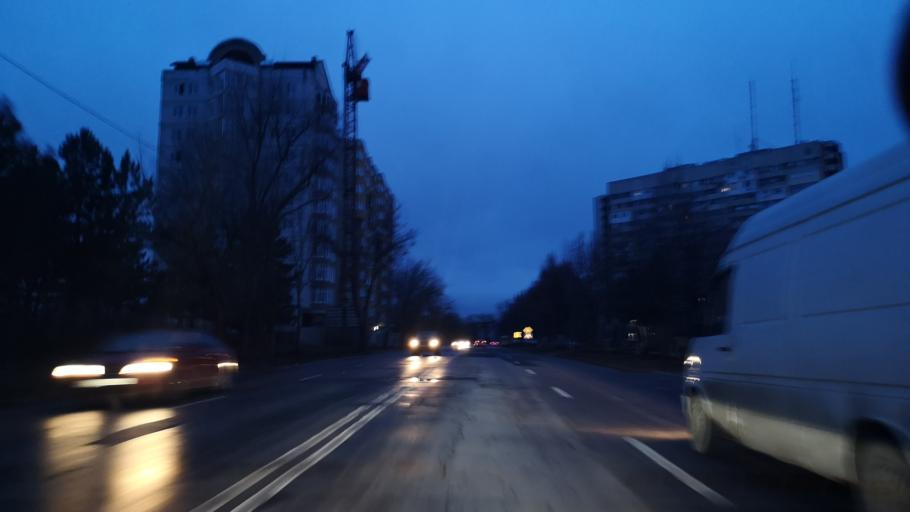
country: MD
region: Chisinau
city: Chisinau
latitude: 47.0312
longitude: 28.8789
